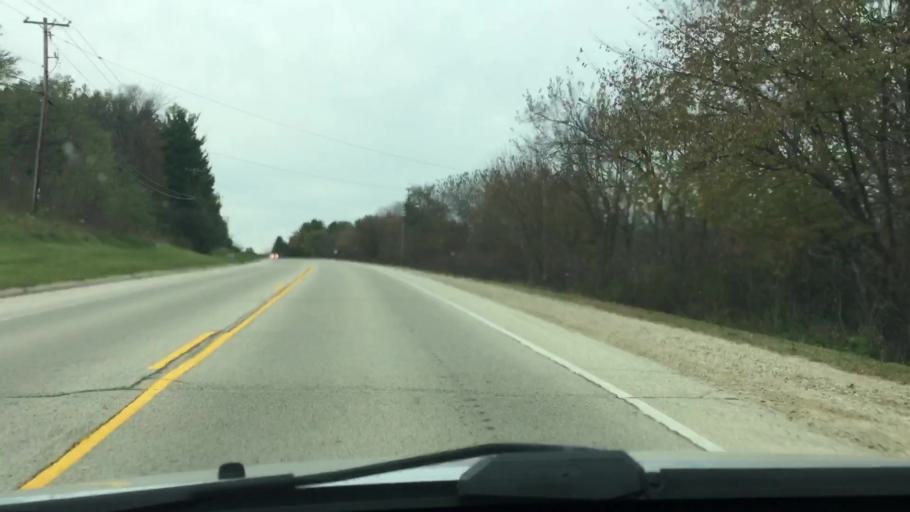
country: US
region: Wisconsin
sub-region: Waukesha County
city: Big Bend
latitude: 42.9000
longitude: -88.2670
